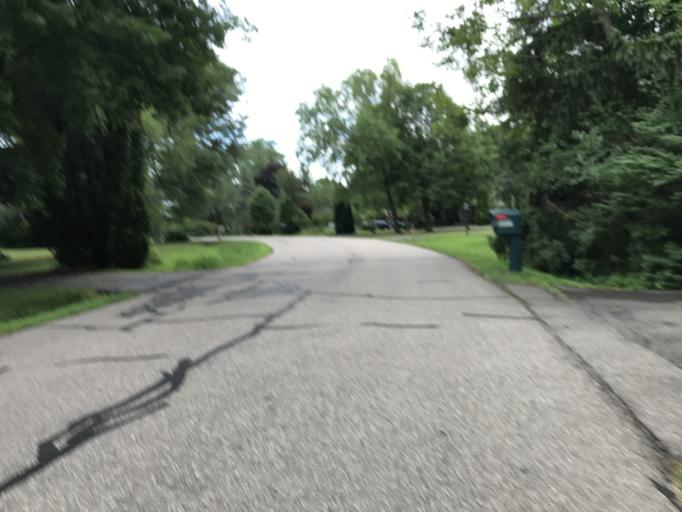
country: US
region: Michigan
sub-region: Oakland County
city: Farmington Hills
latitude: 42.4841
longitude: -83.3459
